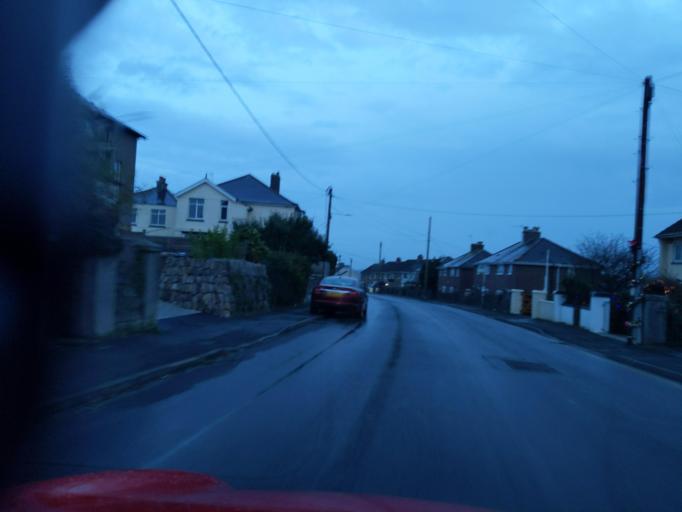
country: GB
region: England
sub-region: Plymouth
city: Plymstock
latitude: 50.3578
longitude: -4.0717
